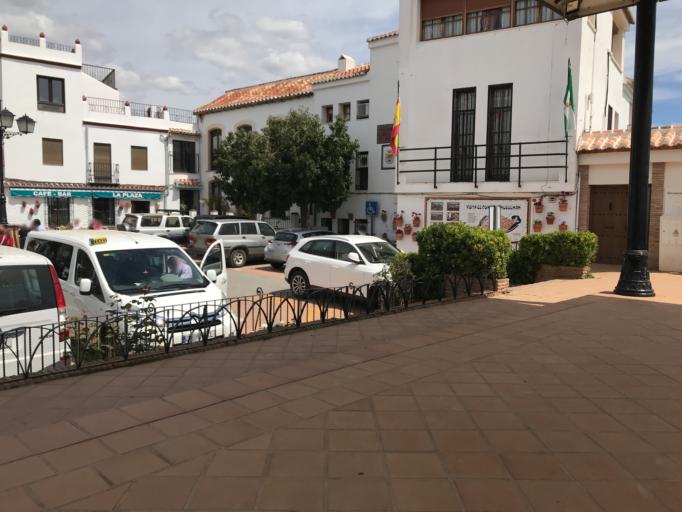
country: ES
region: Andalusia
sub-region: Provincia de Malaga
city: Comares
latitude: 36.8486
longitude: -4.2469
